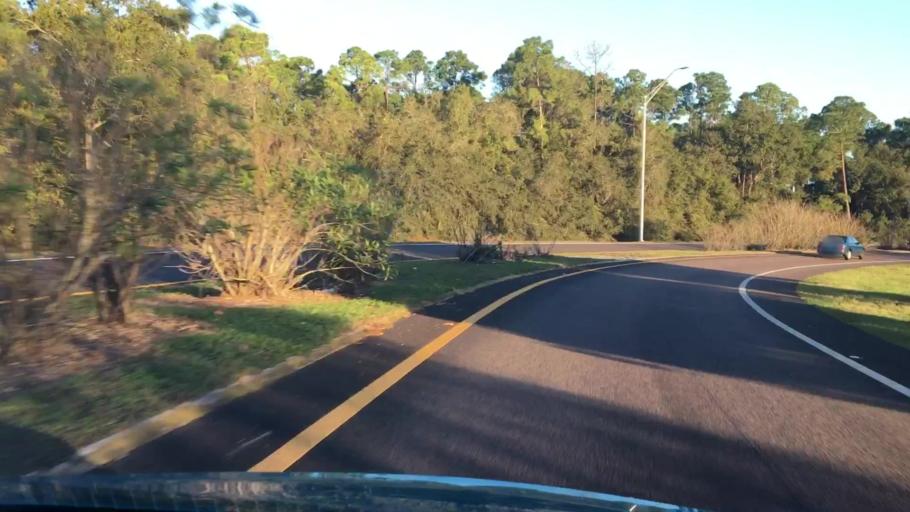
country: US
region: Florida
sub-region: Volusia County
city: DeBary
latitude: 28.8736
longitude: -81.2857
